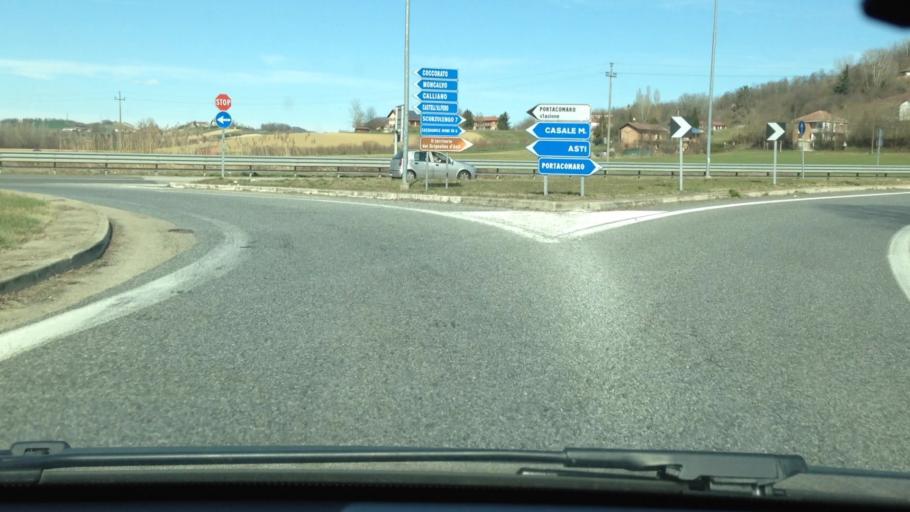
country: IT
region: Piedmont
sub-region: Provincia di Asti
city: Castell'Alfero
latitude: 44.9586
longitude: 8.2298
